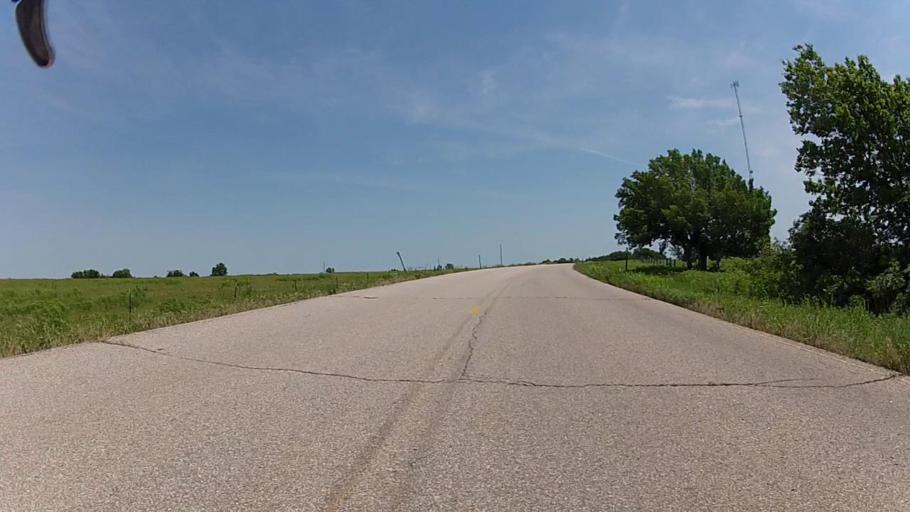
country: US
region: Kansas
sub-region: Chautauqua County
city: Sedan
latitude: 37.1102
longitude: -96.4756
